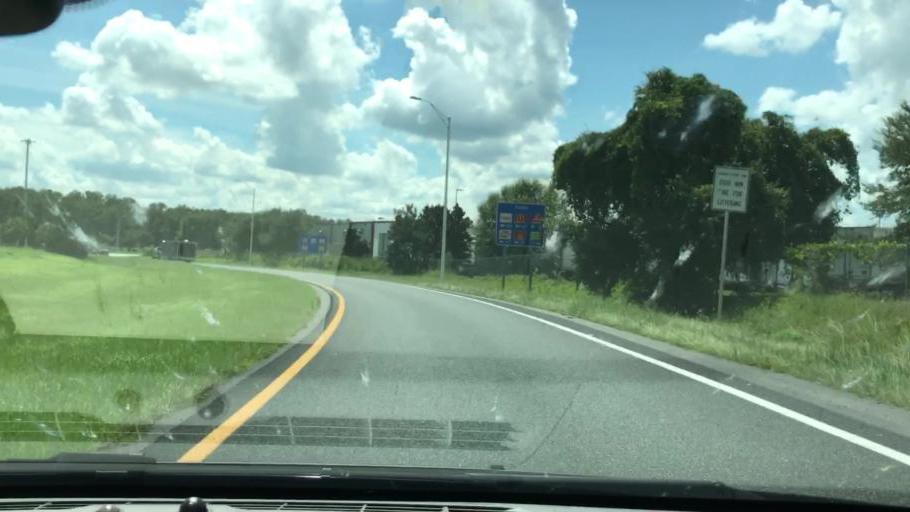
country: US
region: Florida
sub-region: Marion County
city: Ocala
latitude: 29.2693
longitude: -82.1967
